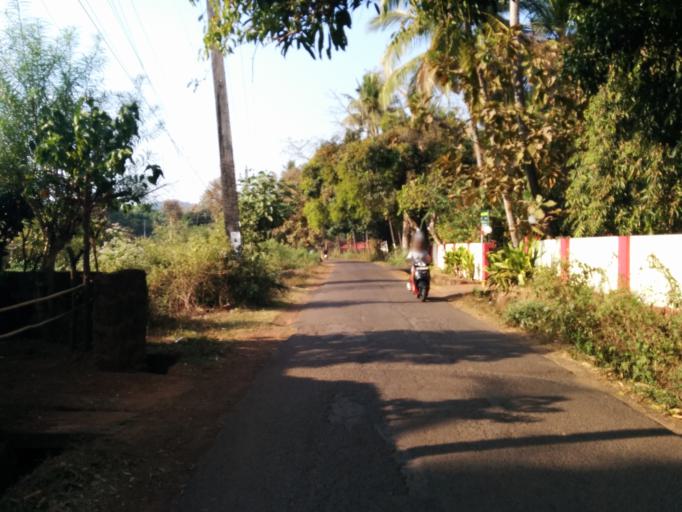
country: IN
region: Karnataka
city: Canacona
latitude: 15.0059
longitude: 74.0314
